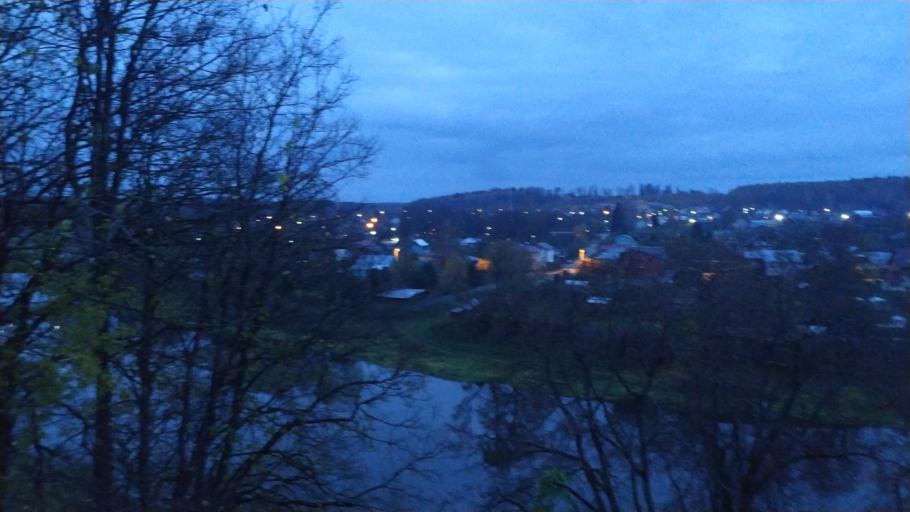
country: RU
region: Moskovskaya
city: Ruza
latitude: 55.6978
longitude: 36.1893
